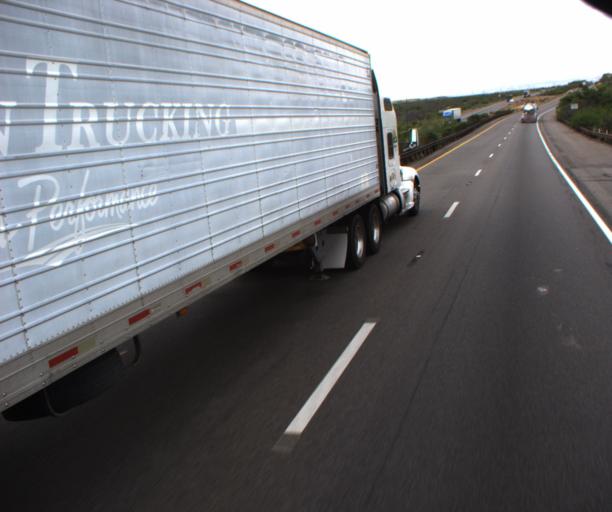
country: US
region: Arizona
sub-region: Cochise County
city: Saint David
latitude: 32.0122
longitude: -110.1241
